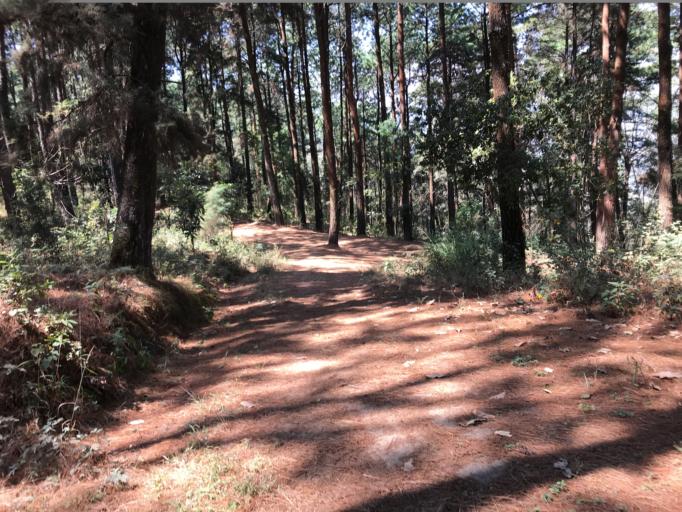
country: GT
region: Guatemala
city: Villa Canales
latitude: 14.4819
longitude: -90.5486
